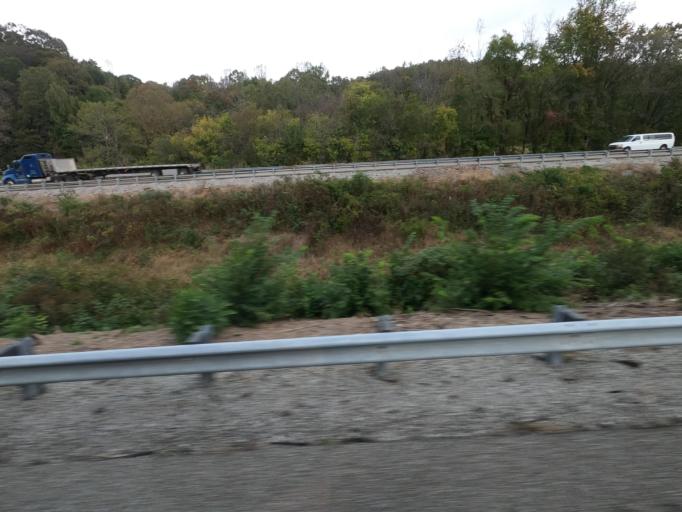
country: US
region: Tennessee
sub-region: Humphreys County
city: Waverly
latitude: 35.8739
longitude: -87.7135
